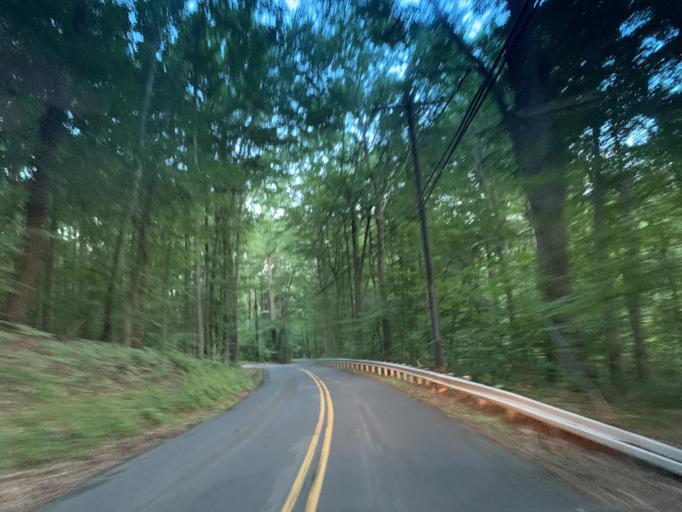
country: US
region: Maryland
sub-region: Harford County
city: Aberdeen
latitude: 39.5358
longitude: -76.1494
